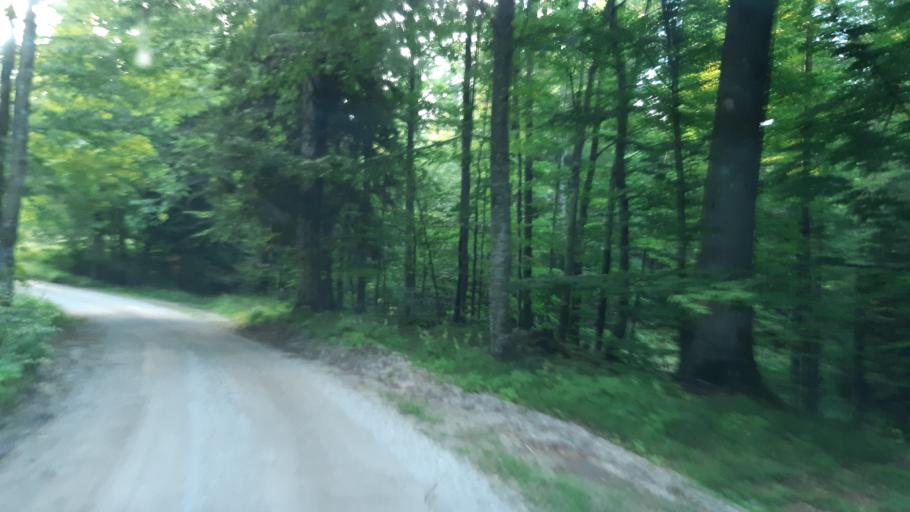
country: SI
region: Dolenjske Toplice
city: Dolenjske Toplice
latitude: 45.6749
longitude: 15.0036
